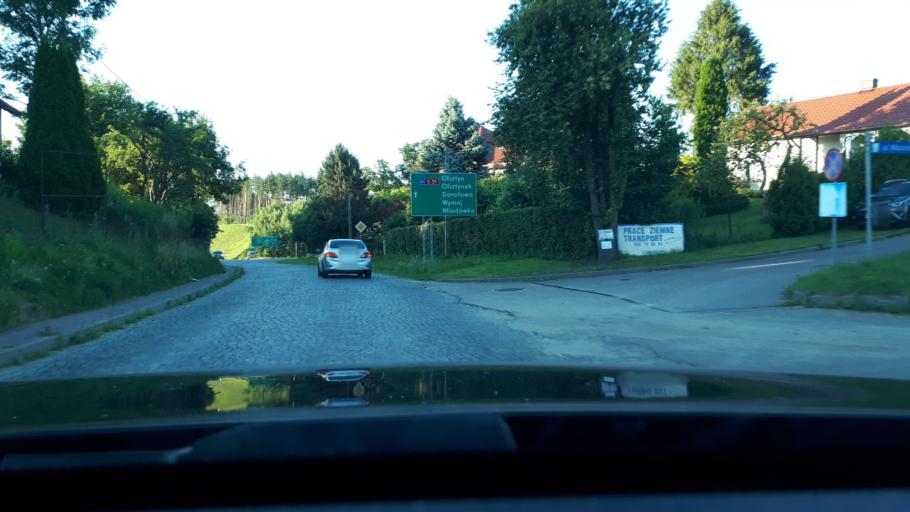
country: PL
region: Warmian-Masurian Voivodeship
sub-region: Powiat olsztynski
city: Stawiguda
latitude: 53.6611
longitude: 20.4011
